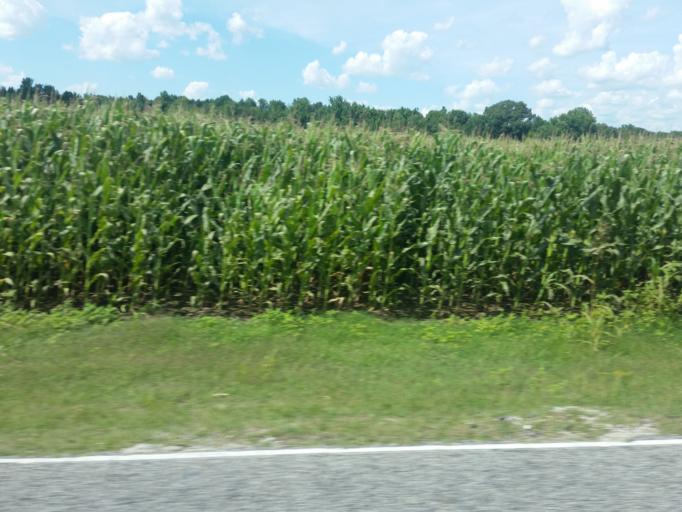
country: US
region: Tennessee
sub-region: Gibson County
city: Milan
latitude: 35.9767
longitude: -88.7540
